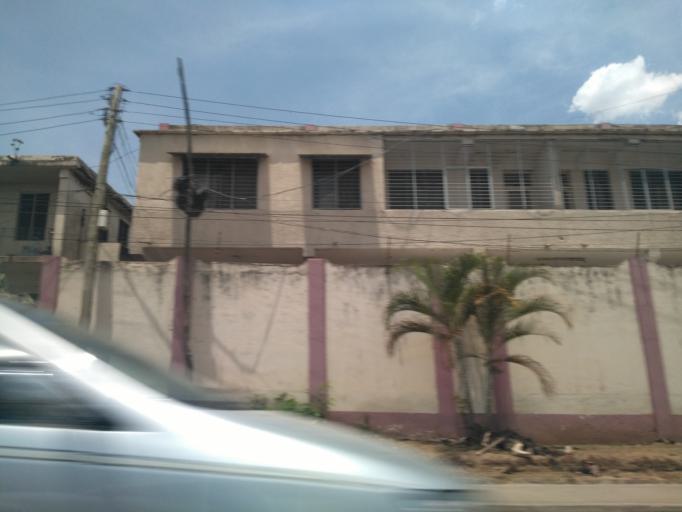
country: TZ
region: Mwanza
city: Mwanza
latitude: -2.5405
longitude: 32.9045
